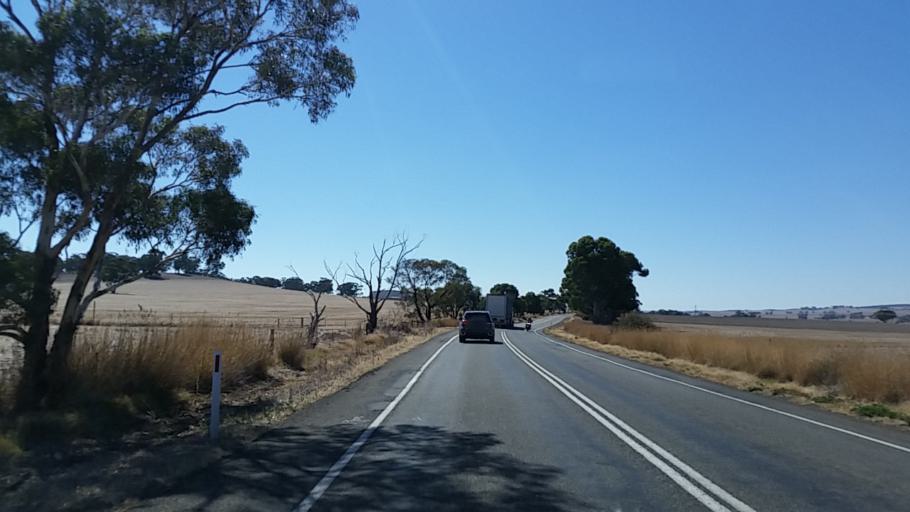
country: AU
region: South Australia
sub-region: Clare and Gilbert Valleys
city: Clare
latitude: -34.0300
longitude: 138.8029
